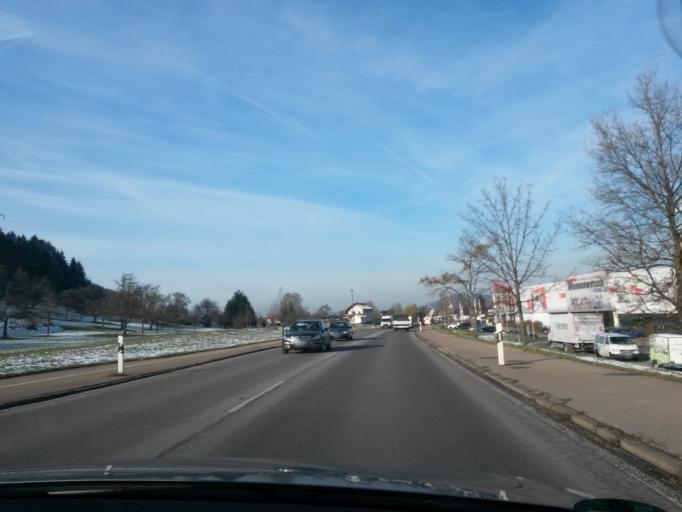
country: DE
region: Baden-Wuerttemberg
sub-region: Regierungsbezirk Stuttgart
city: Gingen an der Fils
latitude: 48.6503
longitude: 9.7839
